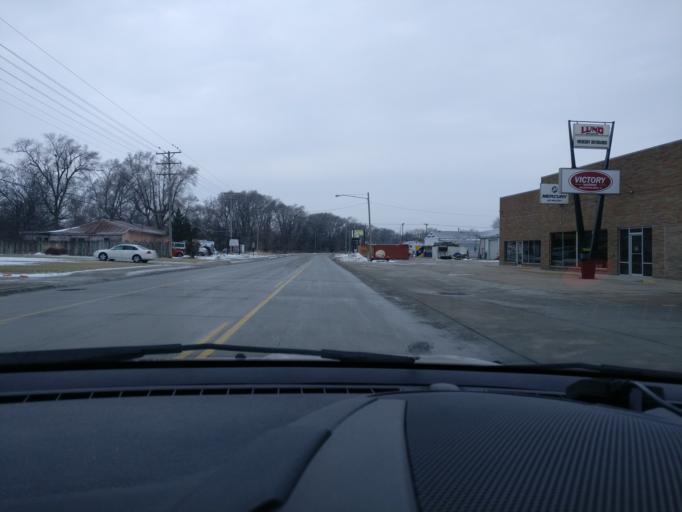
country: US
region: Nebraska
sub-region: Dodge County
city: Fremont
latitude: 41.4370
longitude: -96.5170
